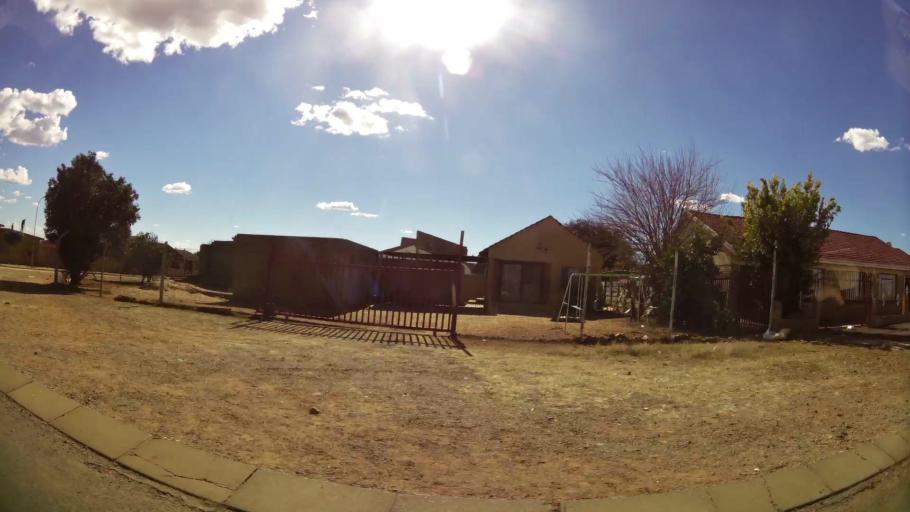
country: ZA
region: North-West
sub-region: Dr Kenneth Kaunda District Municipality
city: Klerksdorp
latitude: -26.8758
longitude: 26.5874
